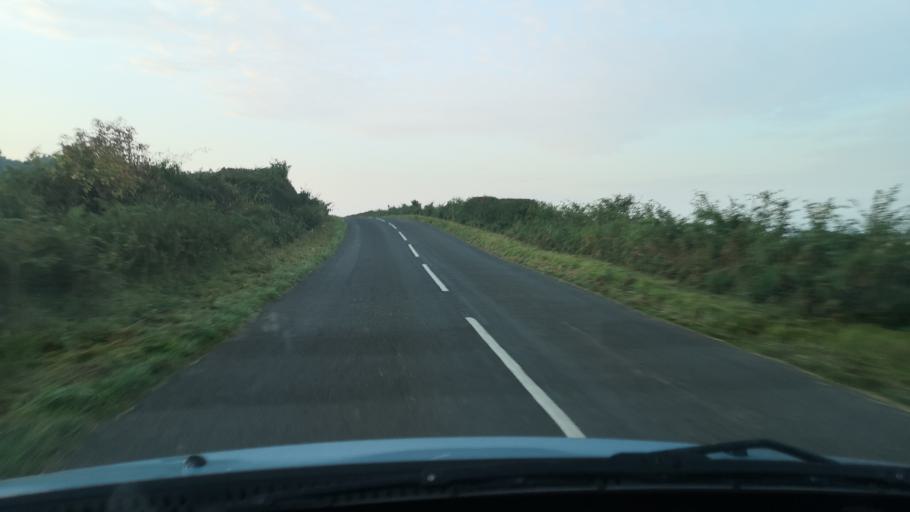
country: GB
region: England
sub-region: City and Borough of Wakefield
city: Darrington
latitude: 53.6640
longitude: -1.2868
